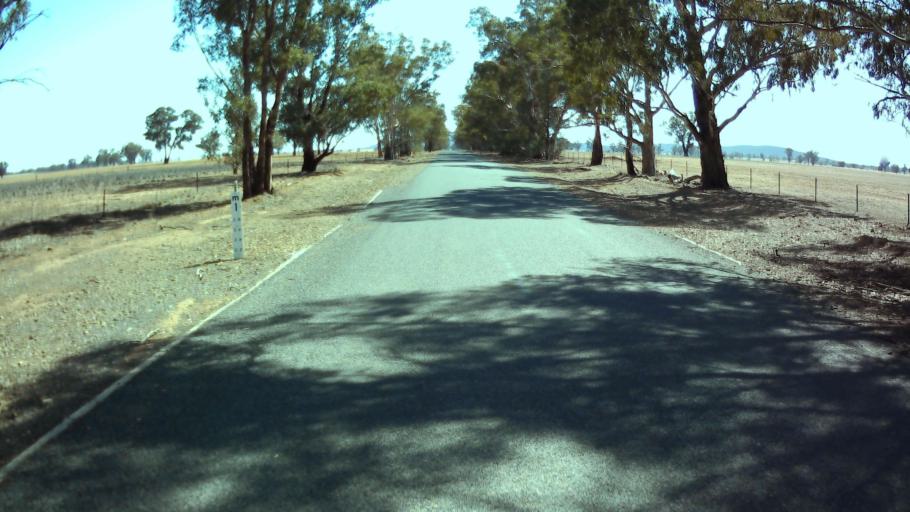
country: AU
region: New South Wales
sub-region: Weddin
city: Grenfell
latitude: -33.7213
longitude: 147.8991
